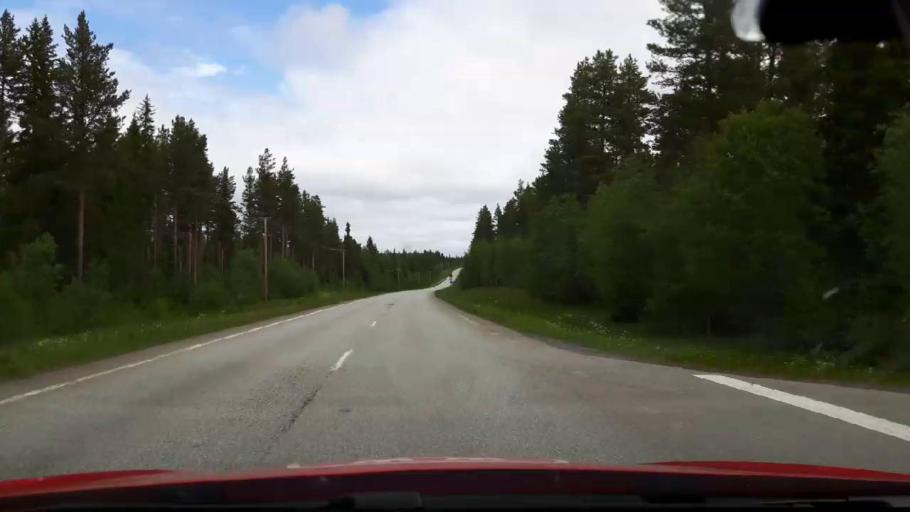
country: SE
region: Jaemtland
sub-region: Krokoms Kommun
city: Krokom
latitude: 63.4590
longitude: 14.4912
